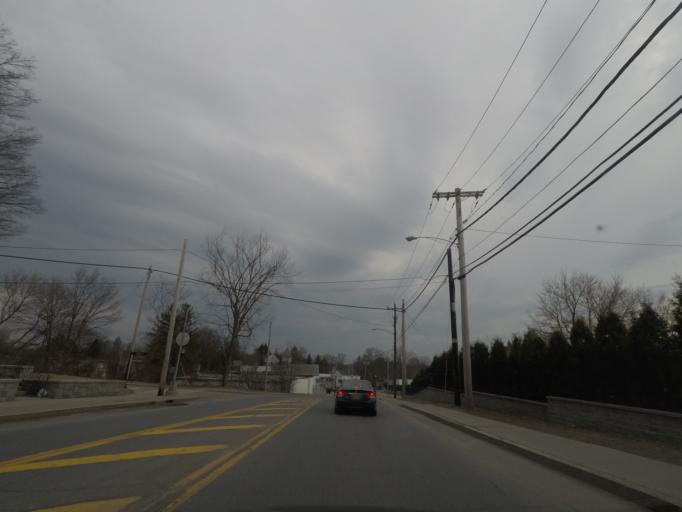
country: US
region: New York
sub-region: Washington County
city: Fort Edward
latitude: 43.2715
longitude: -73.5885
